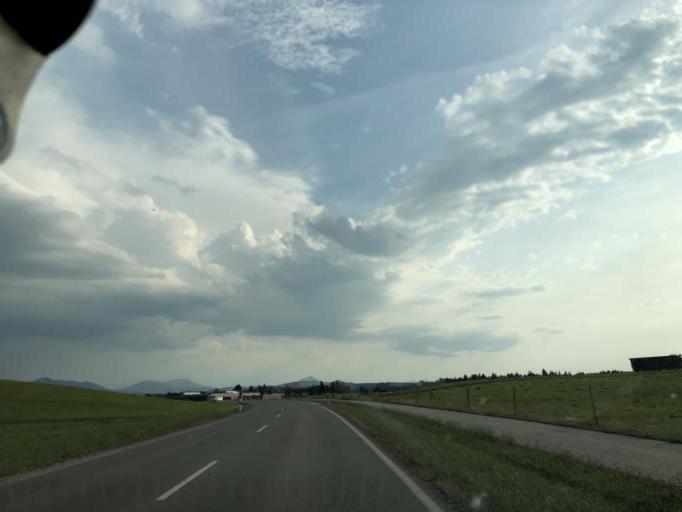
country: DE
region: Bavaria
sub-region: Swabia
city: Gorisried
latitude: 47.7139
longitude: 10.5089
